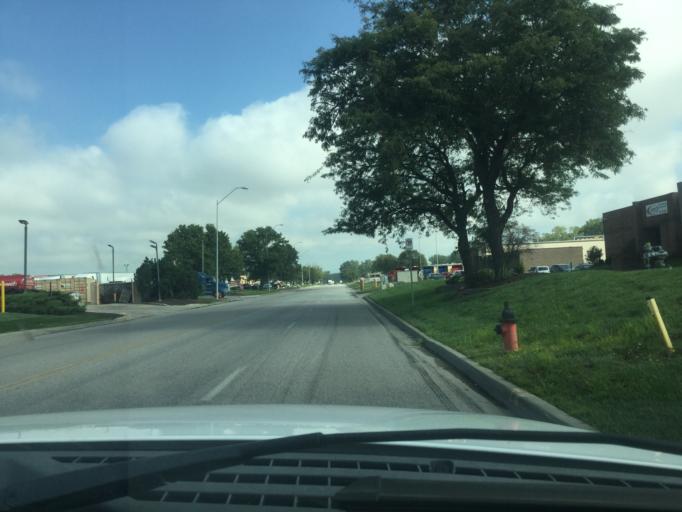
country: US
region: Missouri
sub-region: Jackson County
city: Sugar Creek
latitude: 39.1304
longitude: -94.4962
